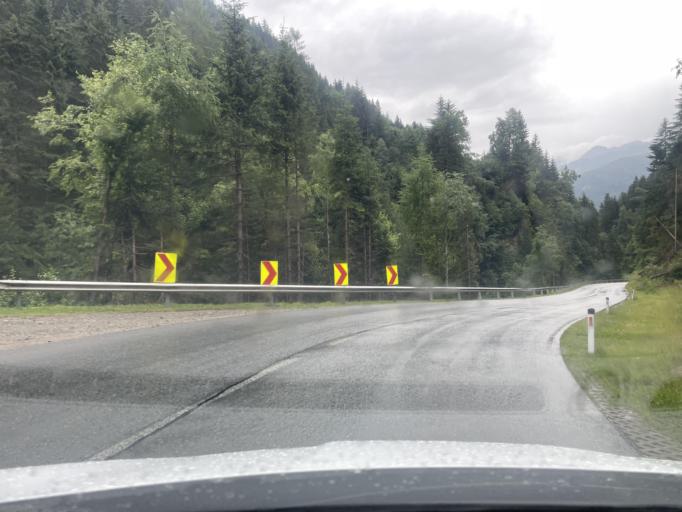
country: AT
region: Tyrol
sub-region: Politischer Bezirk Lienz
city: Sillian
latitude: 46.7635
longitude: 12.4306
